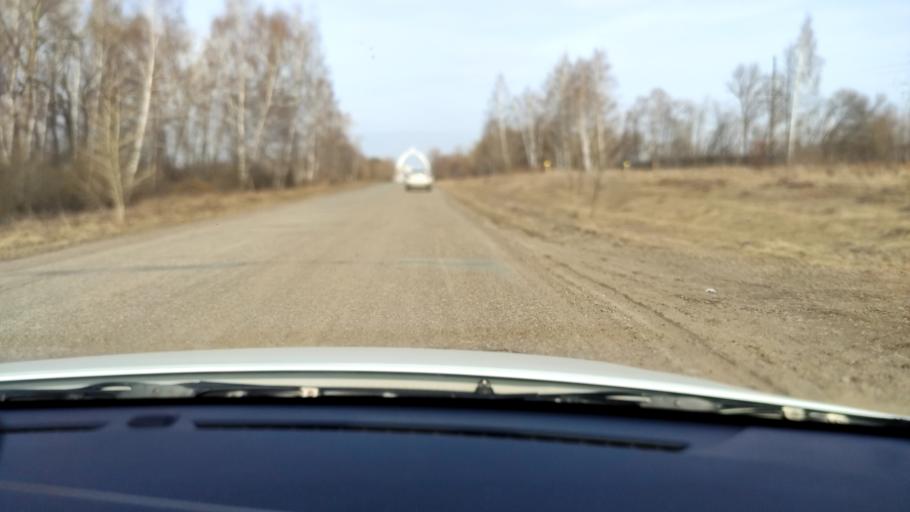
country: RU
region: Tatarstan
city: Stolbishchi
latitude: 55.7222
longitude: 49.2072
